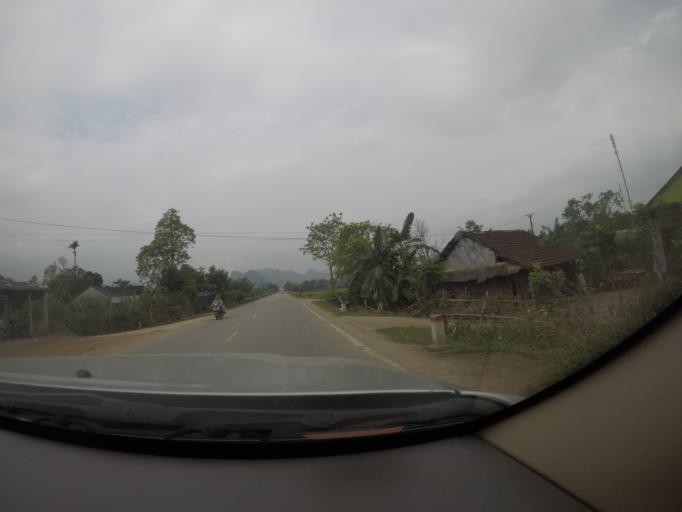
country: VN
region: Quang Binh
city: Ba Don
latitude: 17.6074
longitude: 106.3387
